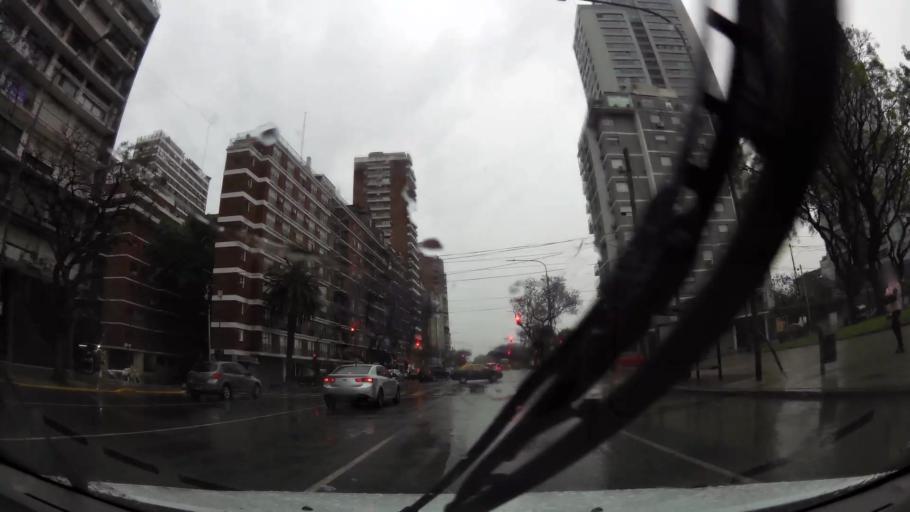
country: AR
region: Buenos Aires F.D.
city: Retiro
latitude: -34.5767
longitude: -58.4046
